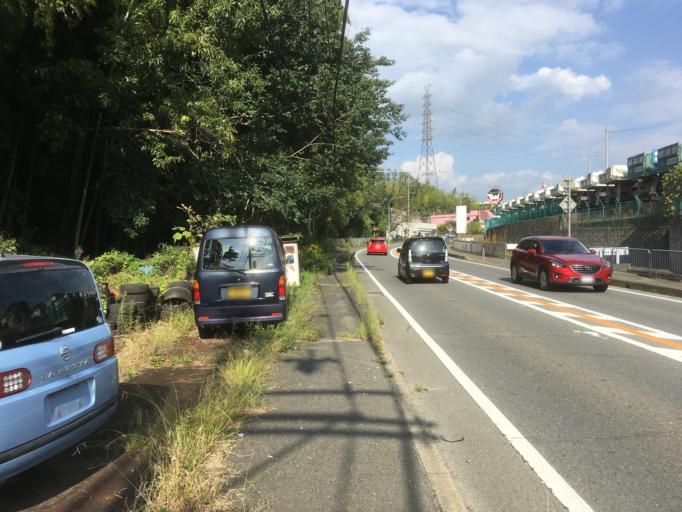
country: JP
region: Nara
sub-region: Ikoma-shi
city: Ikoma
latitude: 34.7303
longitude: 135.7056
